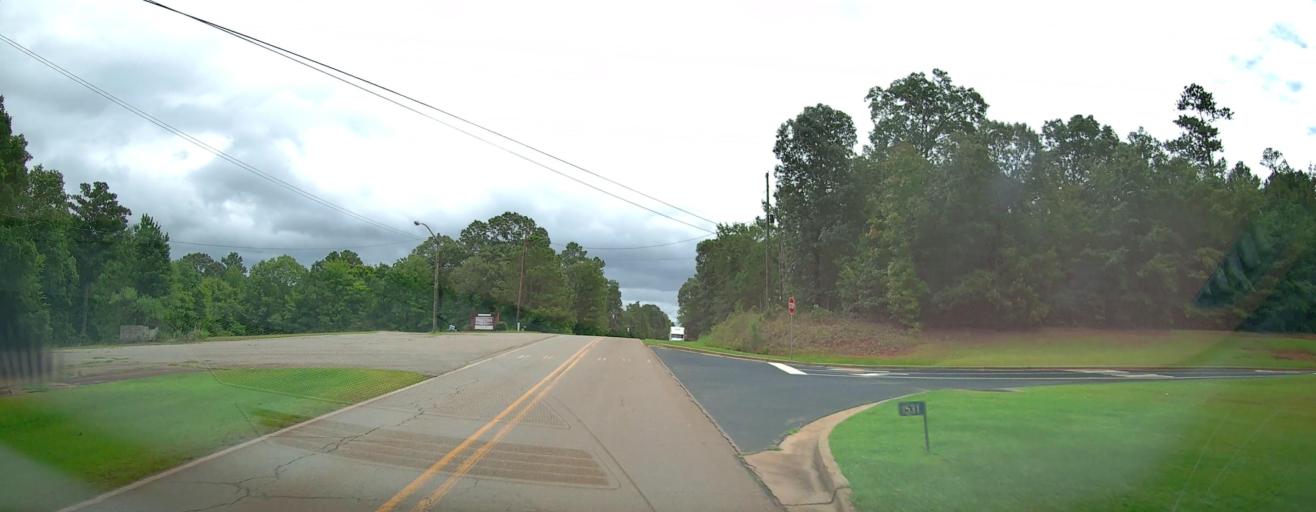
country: US
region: Georgia
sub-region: Bibb County
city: Macon
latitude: 32.7686
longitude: -83.5014
